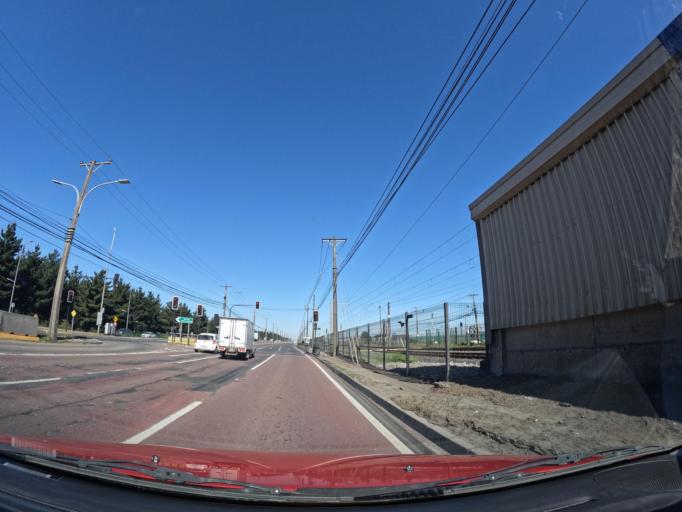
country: CL
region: Biobio
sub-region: Provincia de Concepcion
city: Concepcion
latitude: -36.8549
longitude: -73.1328
